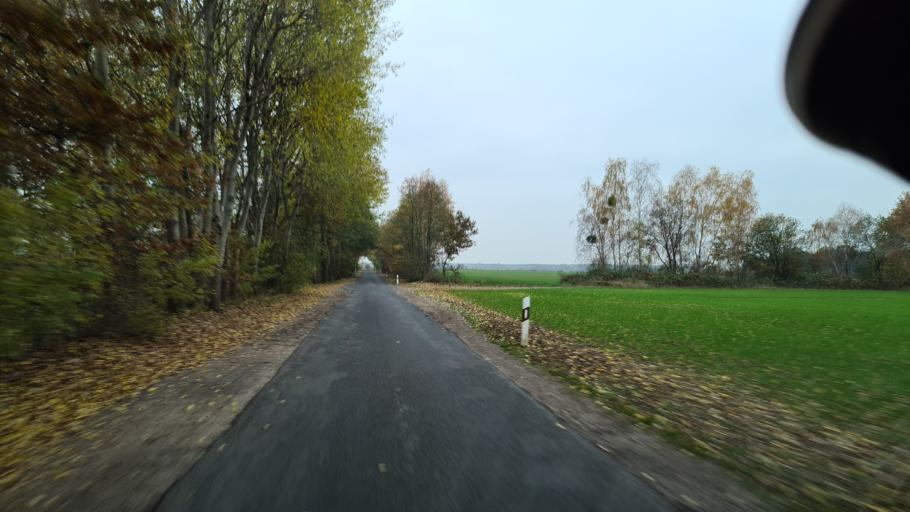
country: DE
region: Brandenburg
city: Ruthnick
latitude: 52.9229
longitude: 12.9975
